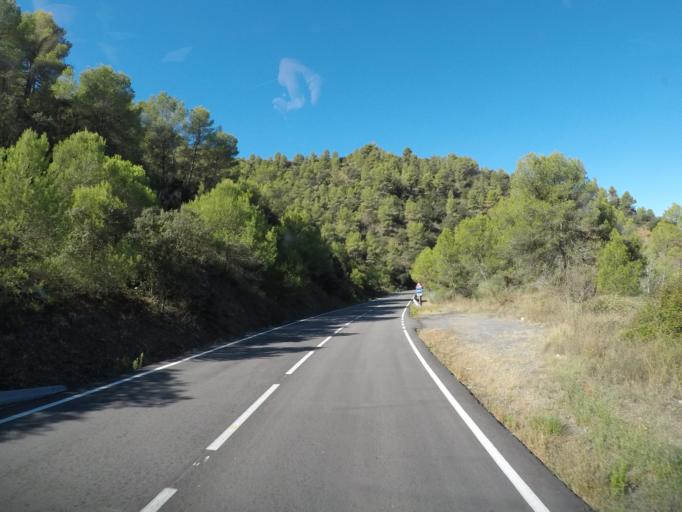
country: ES
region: Catalonia
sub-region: Provincia de Tarragona
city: Falset
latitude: 41.1677
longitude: 0.8086
